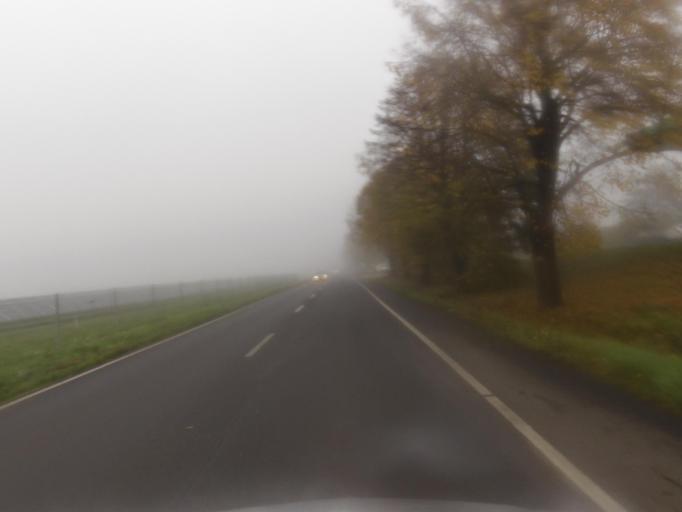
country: CZ
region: Ustecky
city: Libochovice
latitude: 50.4006
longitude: 14.0248
